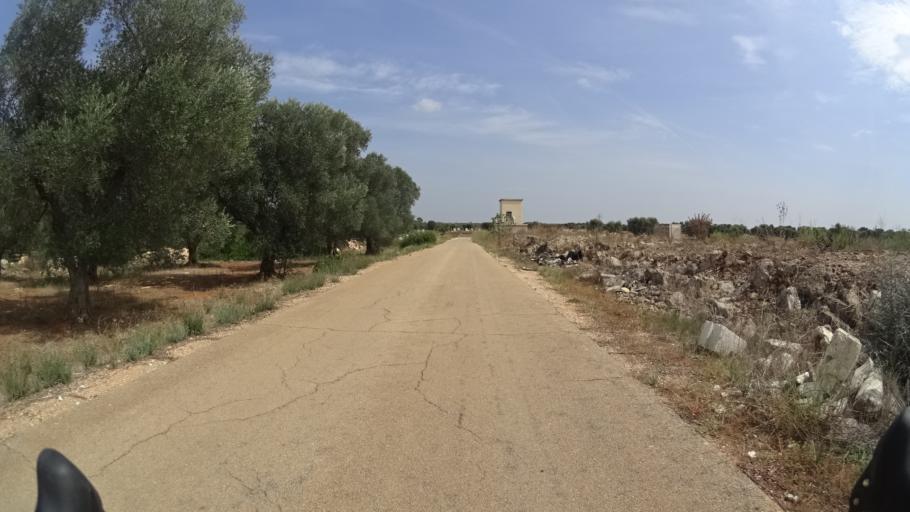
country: IT
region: Apulia
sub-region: Provincia di Brindisi
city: San Pancrazio Salentino
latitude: 40.3459
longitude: 17.8497
